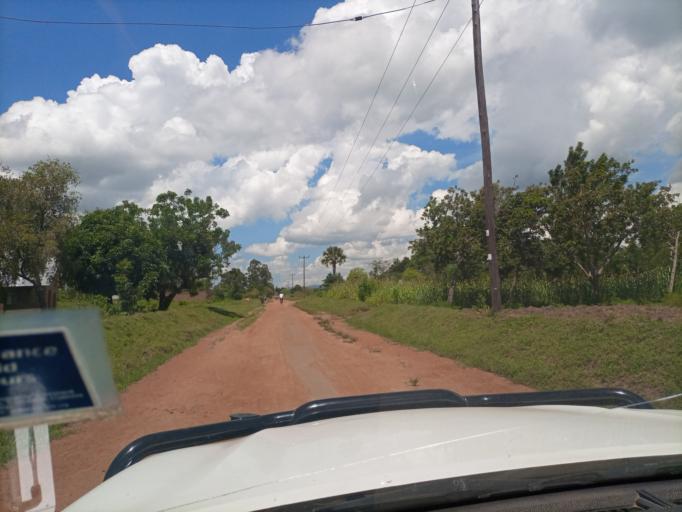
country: UG
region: Eastern Region
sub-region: Tororo District
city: Tororo
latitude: 0.6512
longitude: 33.9975
